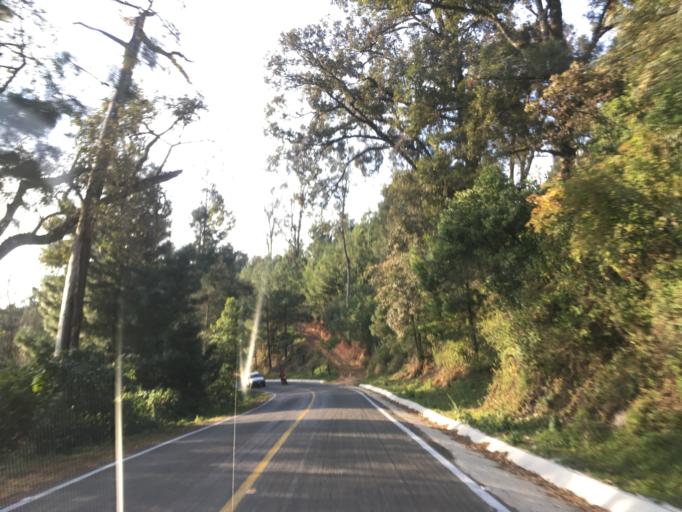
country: MX
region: Michoacan
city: Tzitzio
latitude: 19.6827
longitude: -100.8960
